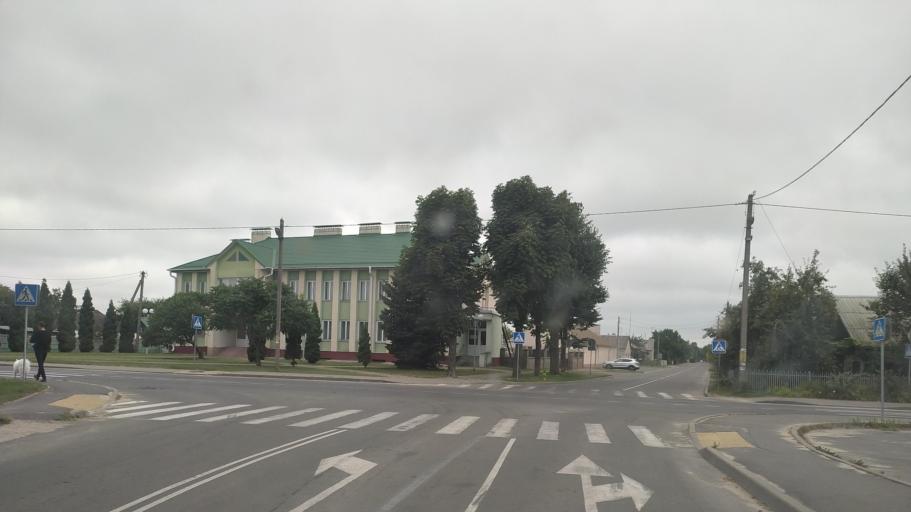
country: BY
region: Brest
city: Byaroza
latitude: 52.5299
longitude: 24.9694
